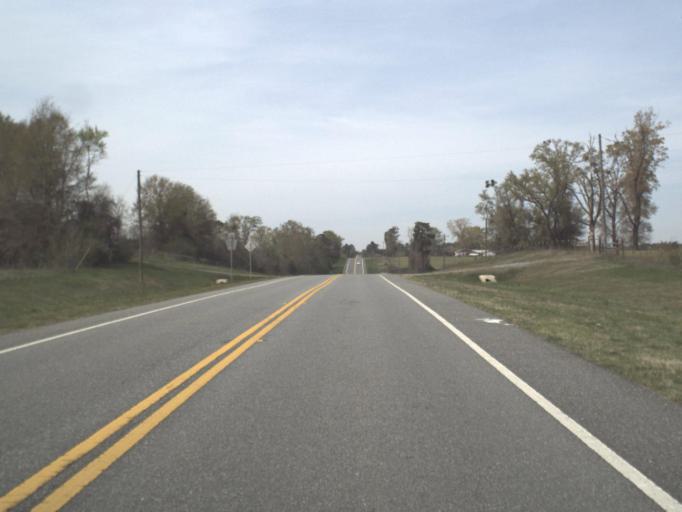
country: US
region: Alabama
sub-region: Geneva County
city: Geneva
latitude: 30.9447
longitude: -85.9763
